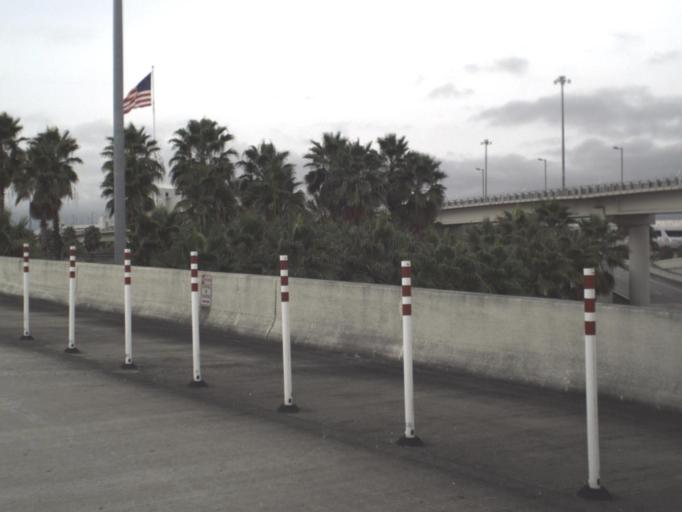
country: US
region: Florida
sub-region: Miami-Dade County
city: Brownsville
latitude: 25.7950
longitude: -80.2626
